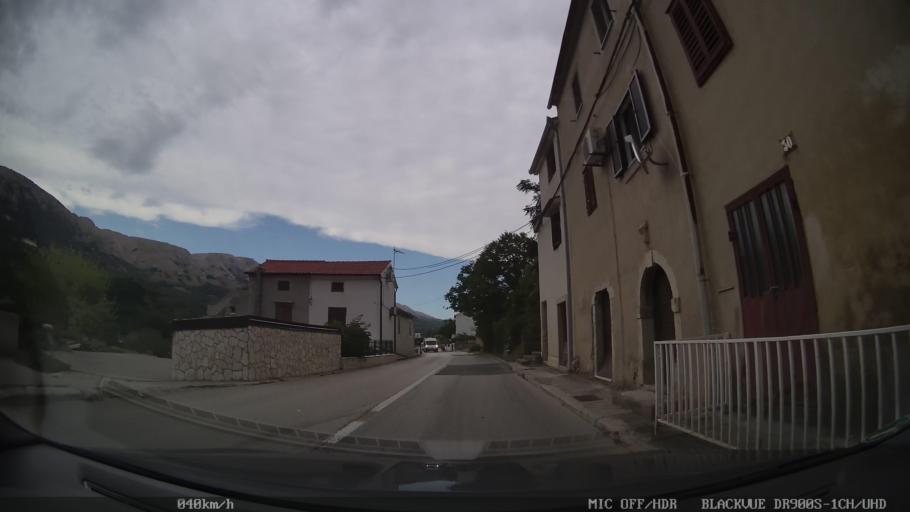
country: HR
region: Primorsko-Goranska
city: Punat
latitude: 44.9792
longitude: 14.7327
